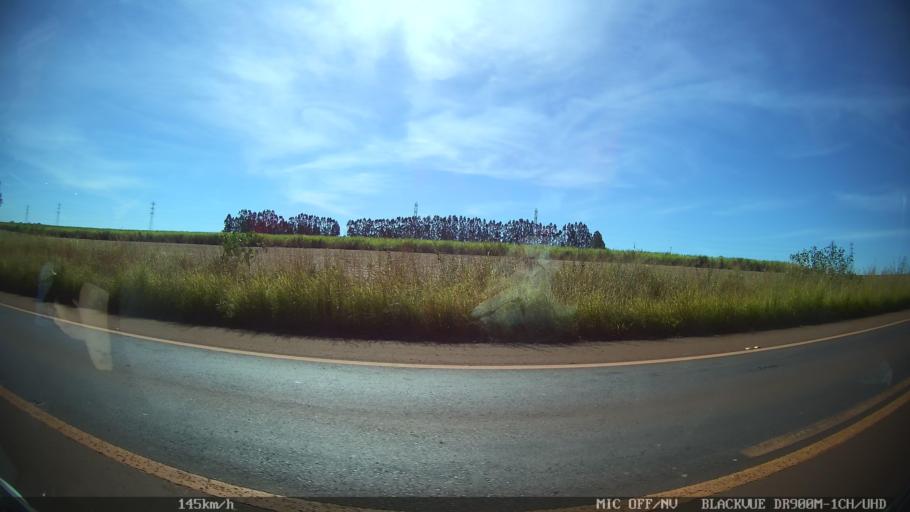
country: BR
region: Sao Paulo
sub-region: Sao Joaquim Da Barra
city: Sao Joaquim da Barra
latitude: -20.5535
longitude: -47.7264
